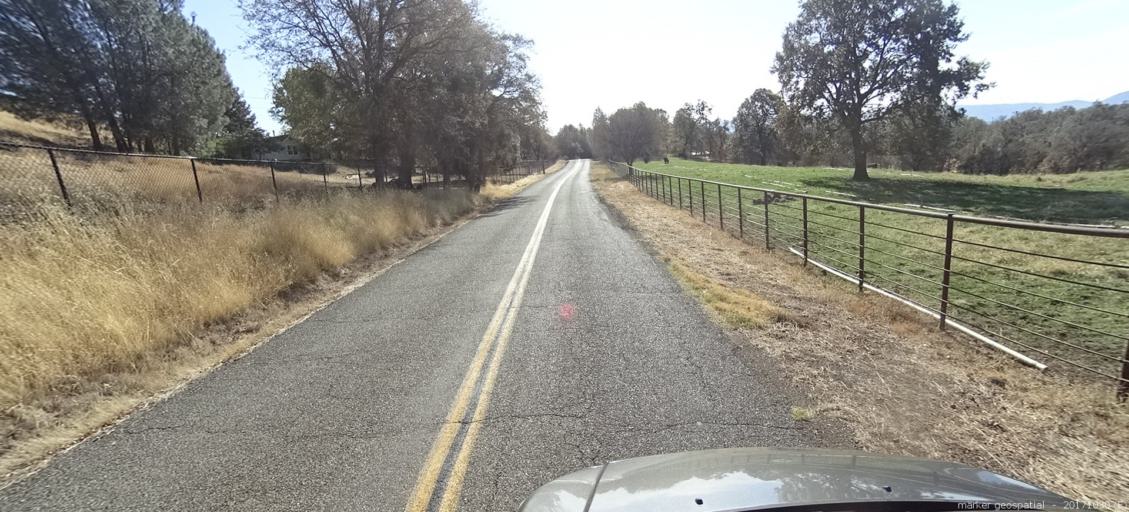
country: US
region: California
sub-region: Shasta County
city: Shingletown
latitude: 40.6489
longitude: -121.9415
